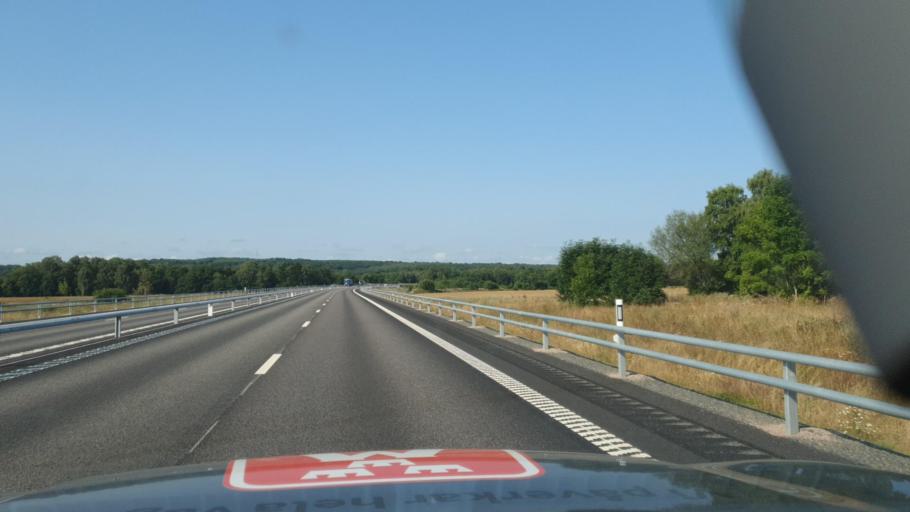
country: SE
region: Skane
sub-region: Kristianstads Kommun
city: Onnestad
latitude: 55.9547
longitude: 13.9215
